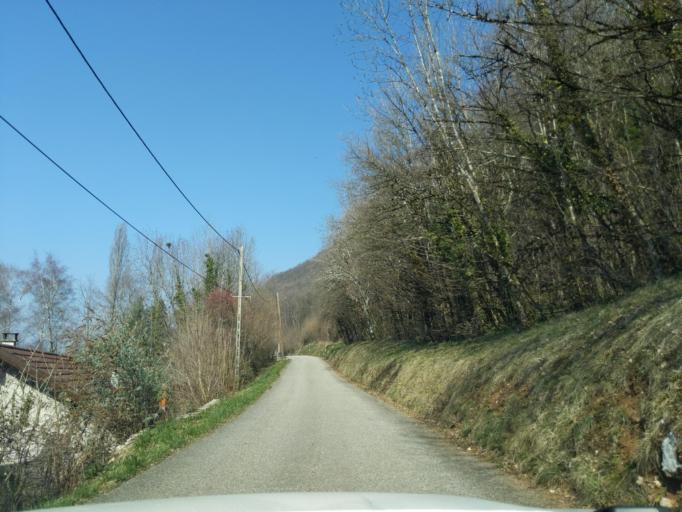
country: FR
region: Rhone-Alpes
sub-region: Departement de la Haute-Savoie
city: Moye
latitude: 45.8972
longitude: 5.8527
